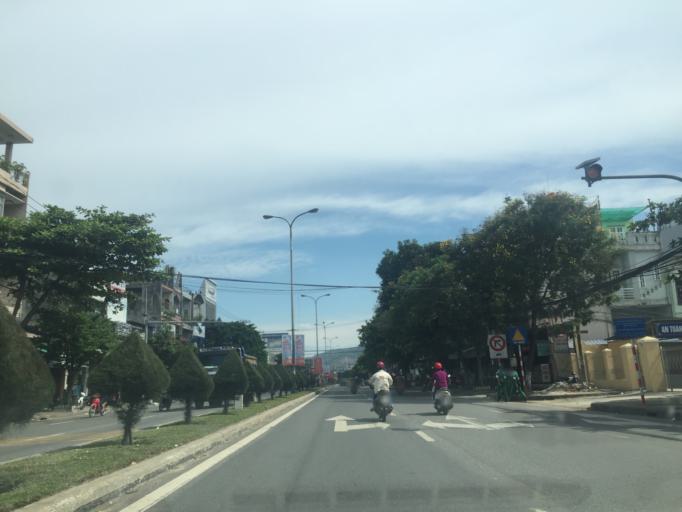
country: VN
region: Da Nang
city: Lien Chieu
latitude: 16.0726
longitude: 108.1501
